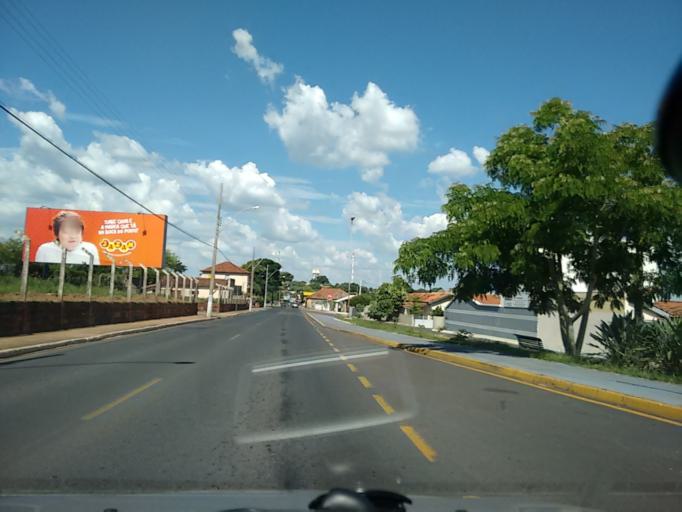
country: BR
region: Sao Paulo
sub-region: Pompeia
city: Pompeia
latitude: -22.1031
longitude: -50.1839
